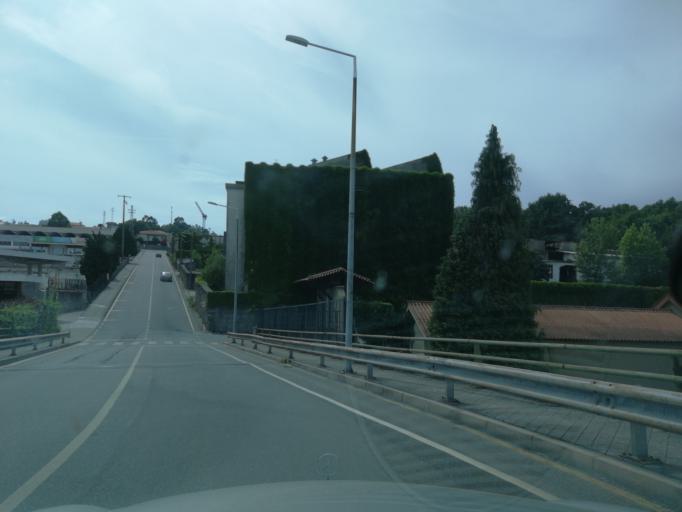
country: PT
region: Braga
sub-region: Vila Nova de Famalicao
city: Calendario
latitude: 41.4076
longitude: -8.5288
